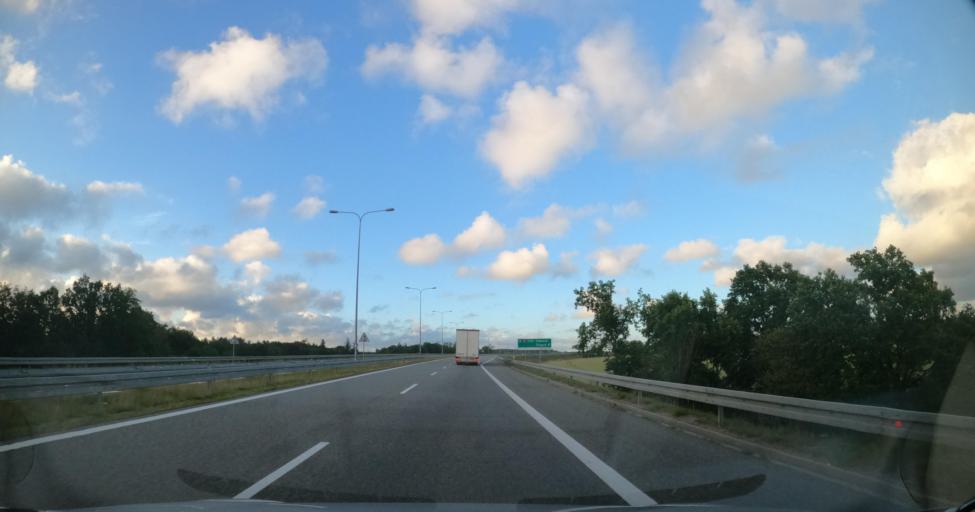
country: PL
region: Pomeranian Voivodeship
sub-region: Slupsk
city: Slupsk
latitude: 54.4664
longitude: 17.1184
